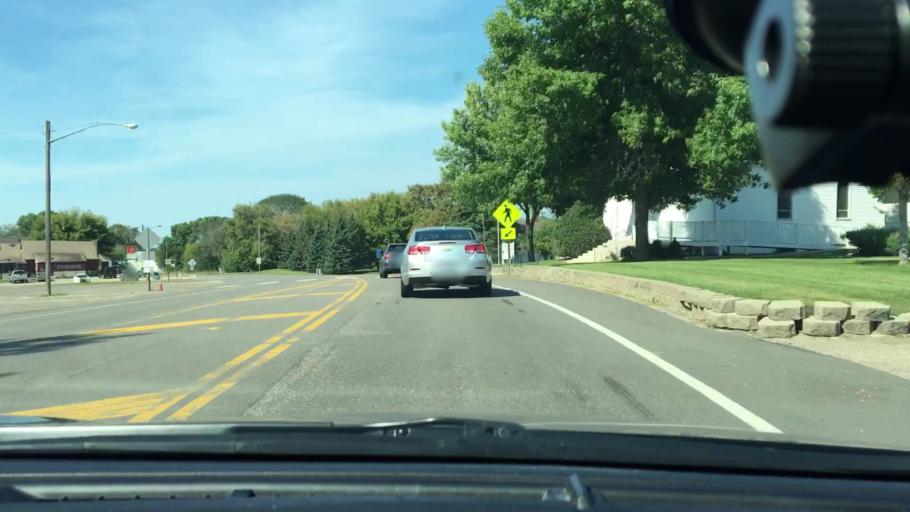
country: US
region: Minnesota
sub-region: Hennepin County
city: Corcoran
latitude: 45.0945
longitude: -93.5445
